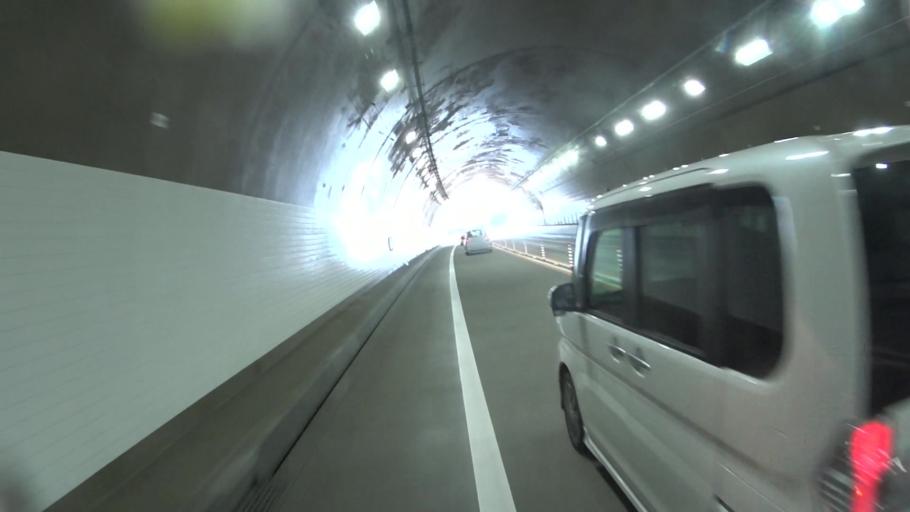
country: JP
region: Kyoto
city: Ayabe
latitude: 35.2530
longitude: 135.3421
